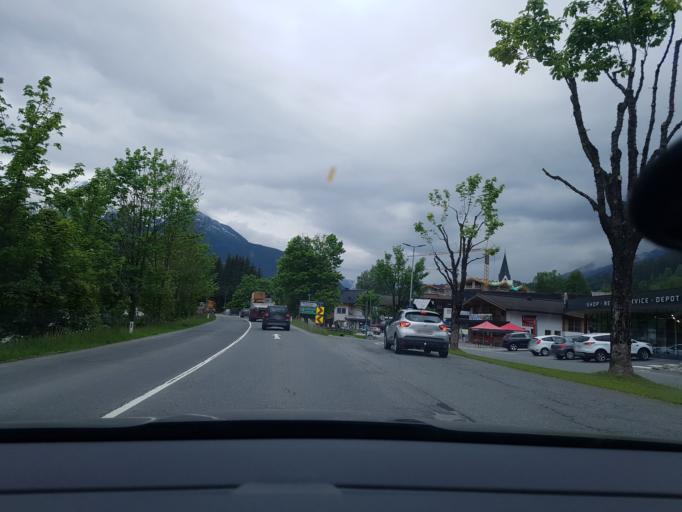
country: AT
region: Salzburg
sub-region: Politischer Bezirk Zell am See
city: Neukirchen am Grossvenediger
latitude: 47.2542
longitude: 12.2822
